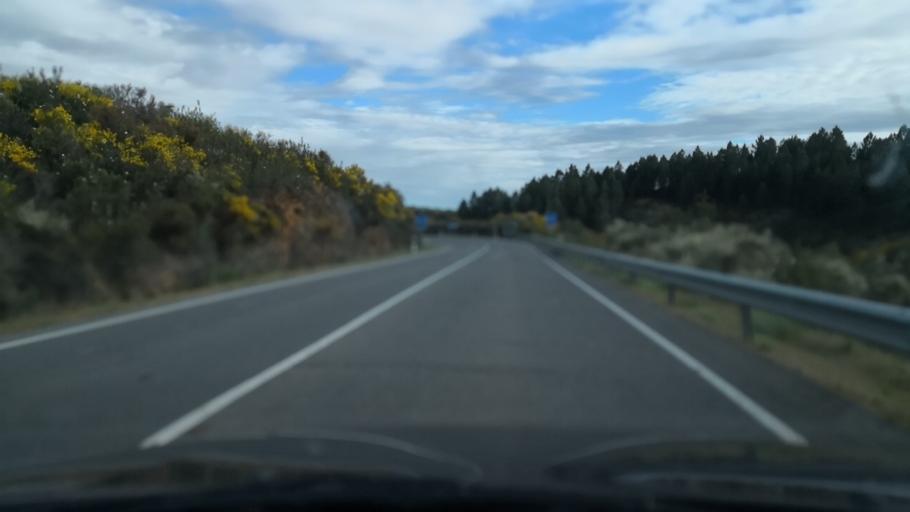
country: ES
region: Extremadura
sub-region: Provincia de Caceres
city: Perales del Puerto
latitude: 40.1316
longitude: -6.6795
